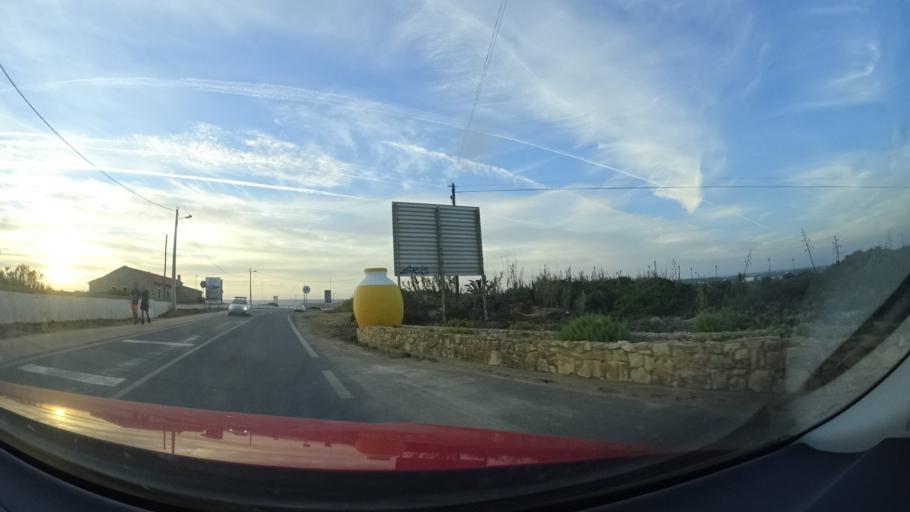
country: PT
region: Faro
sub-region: Vila do Bispo
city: Sagres
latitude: 37.0087
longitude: -8.9476
